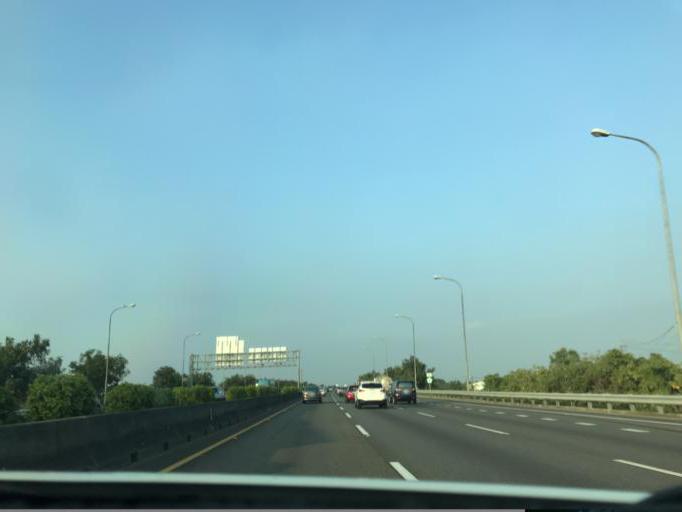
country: TW
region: Taiwan
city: Xinying
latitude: 23.2255
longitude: 120.2413
